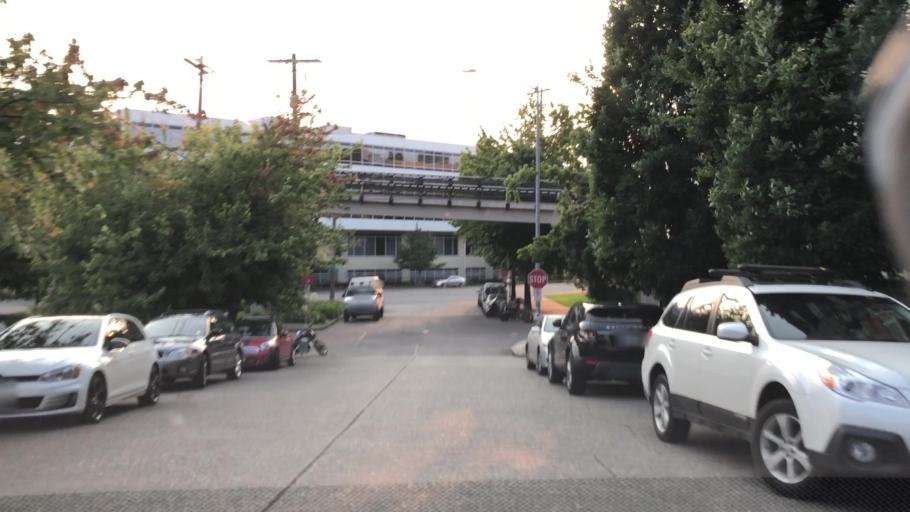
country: US
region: Washington
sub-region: King County
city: Seattle
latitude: 47.6210
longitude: -122.3600
